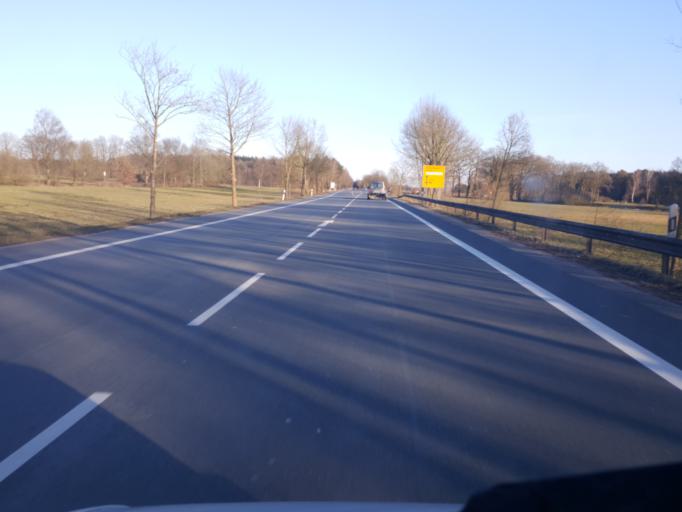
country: DE
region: North Rhine-Westphalia
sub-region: Regierungsbezirk Detmold
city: Hille
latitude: 52.3888
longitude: 8.7209
